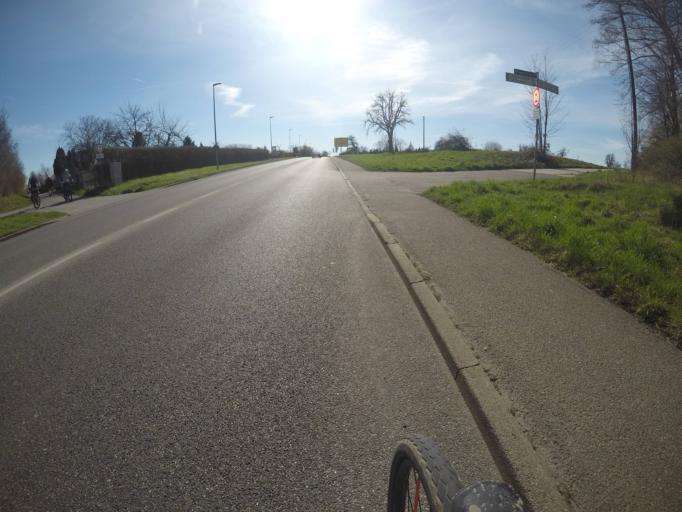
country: DE
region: Baden-Wuerttemberg
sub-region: Regierungsbezirk Stuttgart
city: Stuttgart Muehlhausen
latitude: 48.8290
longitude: 9.2559
